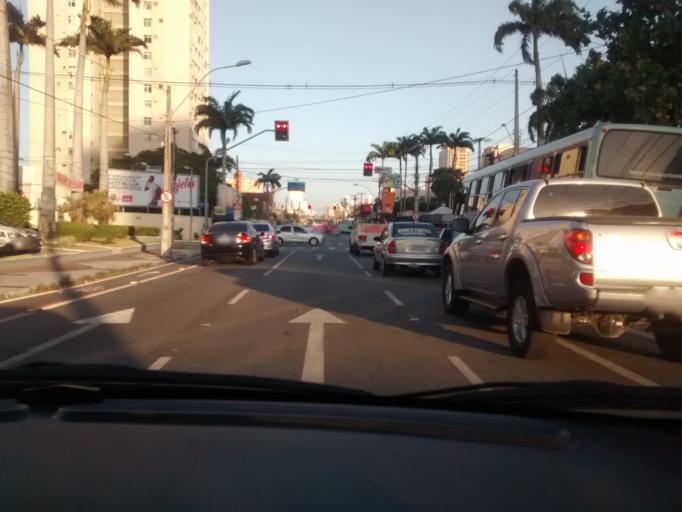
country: BR
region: Ceara
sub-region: Fortaleza
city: Fortaleza
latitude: -3.7383
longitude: -38.4920
